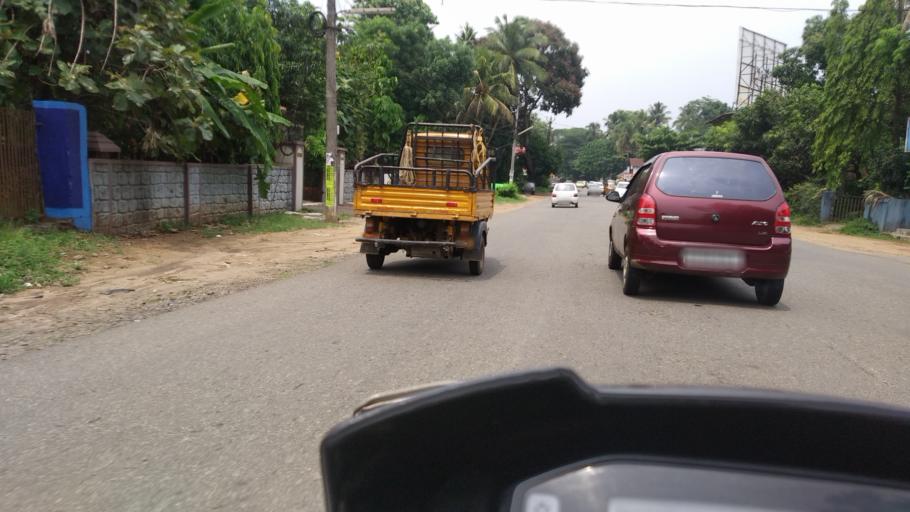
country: IN
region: Kerala
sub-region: Ernakulam
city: Perumpavur
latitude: 10.1134
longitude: 76.5071
